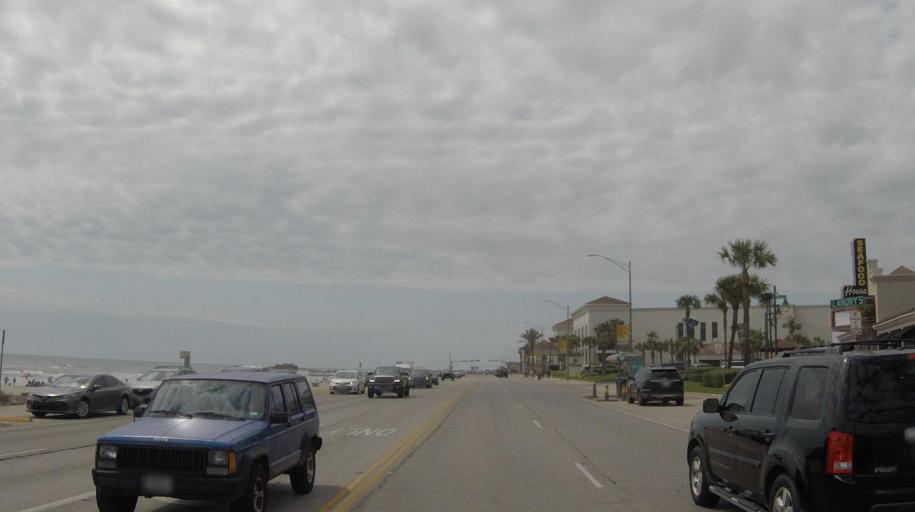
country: US
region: Texas
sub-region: Galveston County
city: Galveston
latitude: 29.2707
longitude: -94.8195
